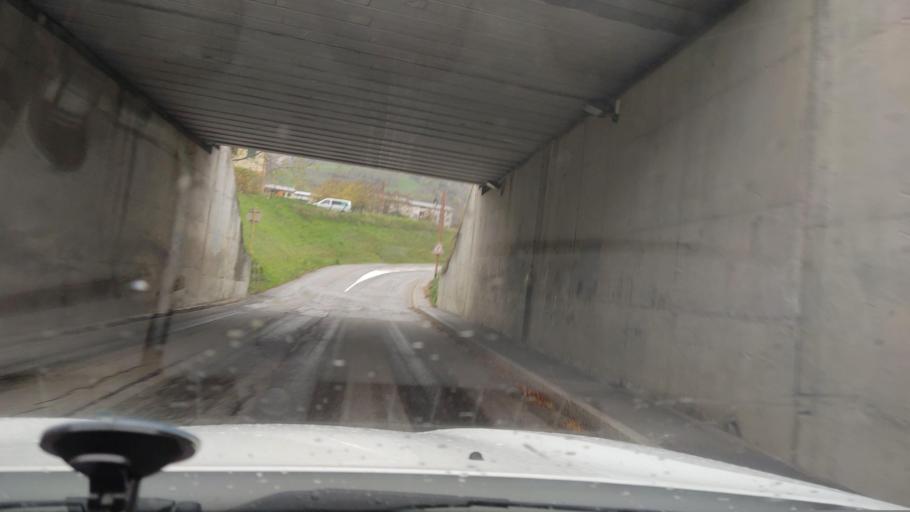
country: FR
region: Rhone-Alpes
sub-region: Departement de la Savoie
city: Bourg-Saint-Maurice
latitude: 45.6124
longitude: 6.7725
